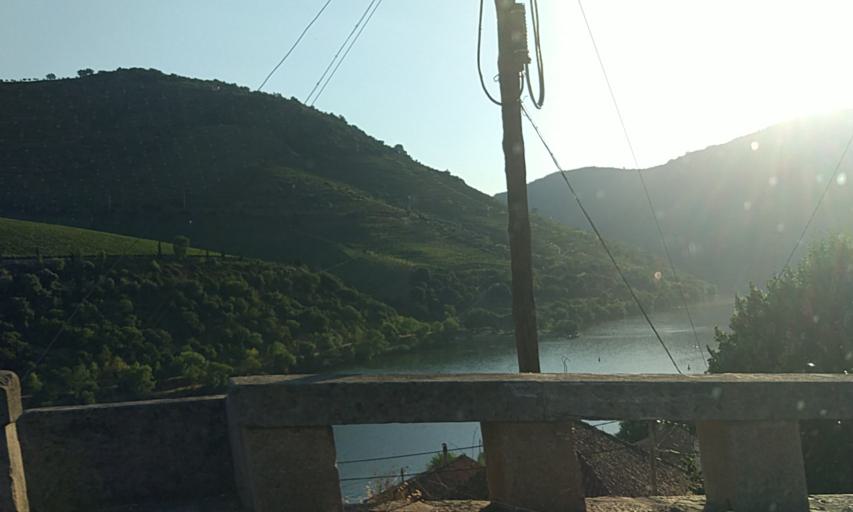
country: PT
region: Viseu
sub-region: Sao Joao da Pesqueira
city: Sao Joao da Pesqueira
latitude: 41.2125
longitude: -7.4247
